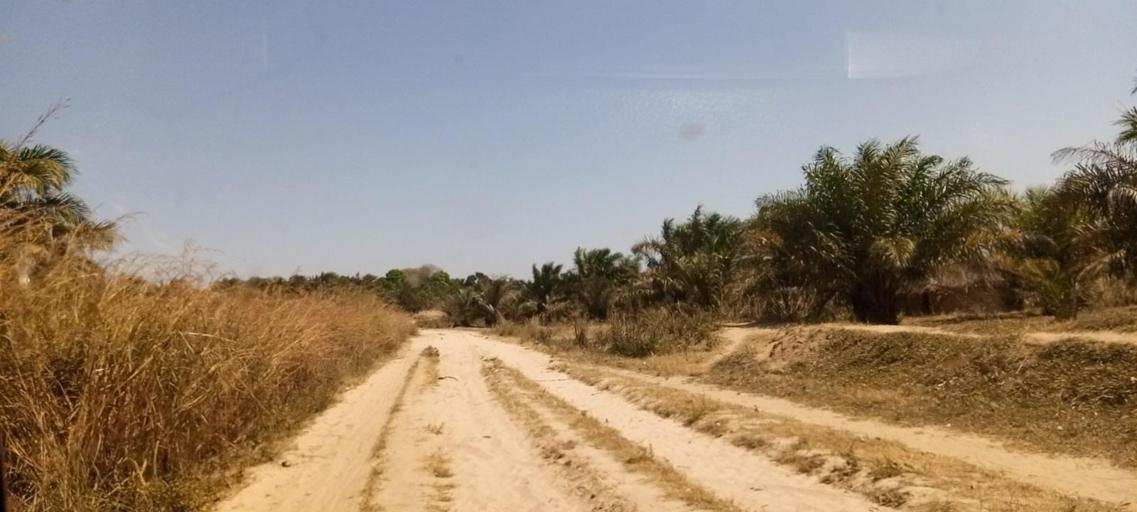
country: CD
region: Kasai-Oriental
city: Kabinda
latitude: -5.9577
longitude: 24.7916
